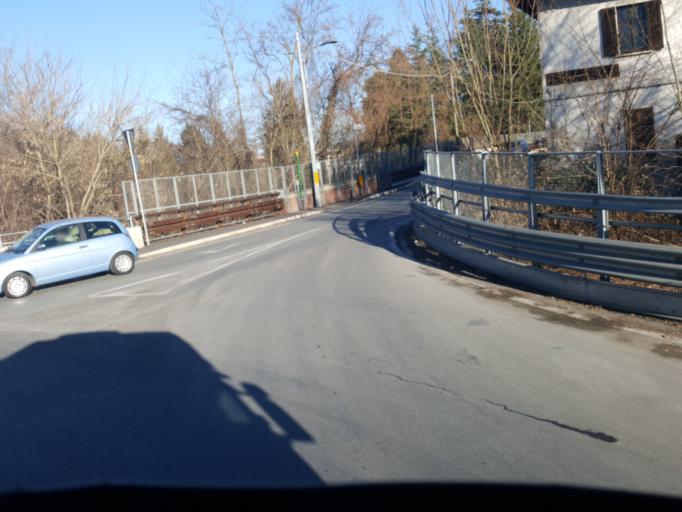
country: IT
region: Piedmont
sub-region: Provincia di Novara
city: Castelletto Sopra Ticino
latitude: 45.7197
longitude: 8.6257
